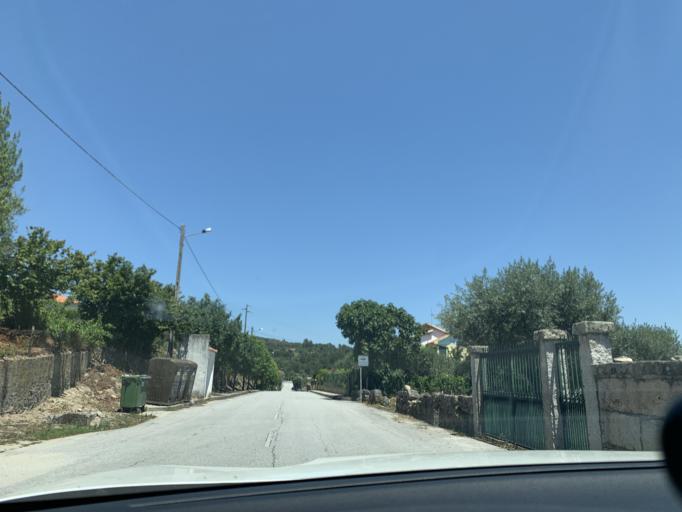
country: PT
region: Guarda
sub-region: Fornos de Algodres
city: Fornos de Algodres
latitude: 40.5758
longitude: -7.6428
